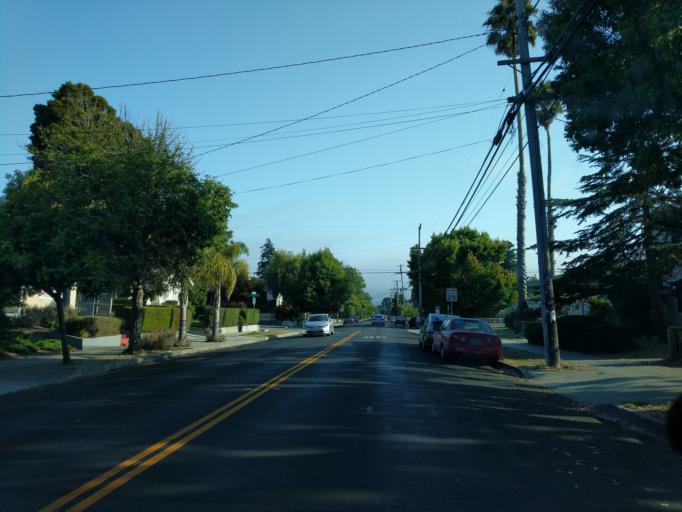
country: US
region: California
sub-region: Santa Cruz County
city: Twin Lakes
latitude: 36.9738
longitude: -122.0082
